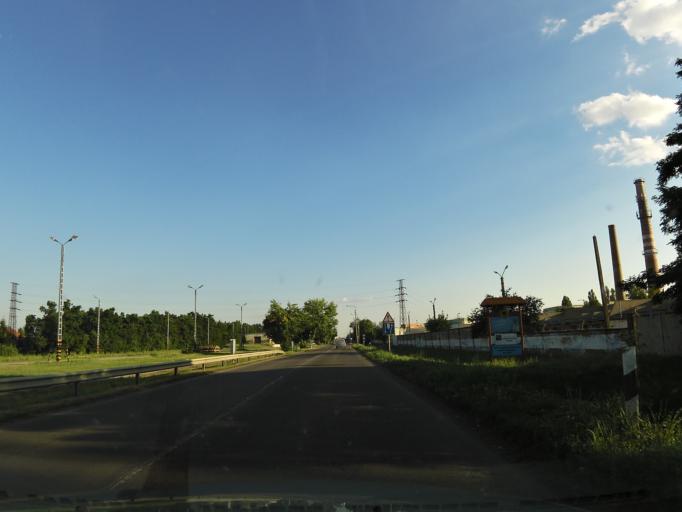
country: HU
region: Jasz-Nagykun-Szolnok
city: Rakocziujfalu
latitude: 47.0232
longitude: 20.2918
